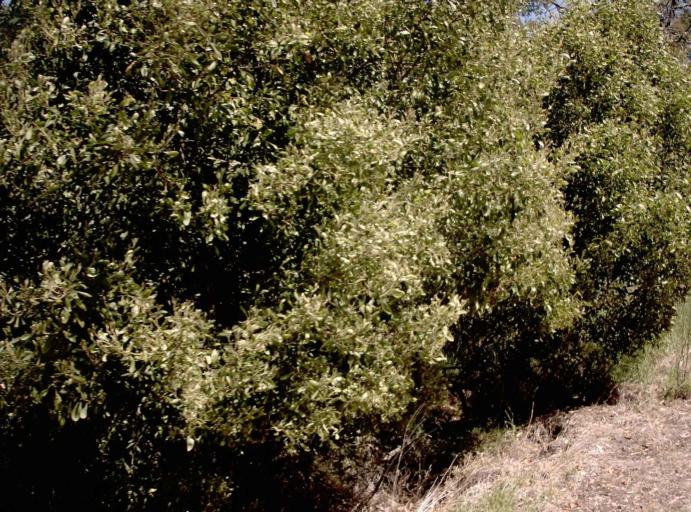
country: AU
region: Victoria
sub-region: East Gippsland
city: Lakes Entrance
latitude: -37.3412
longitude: 148.2286
